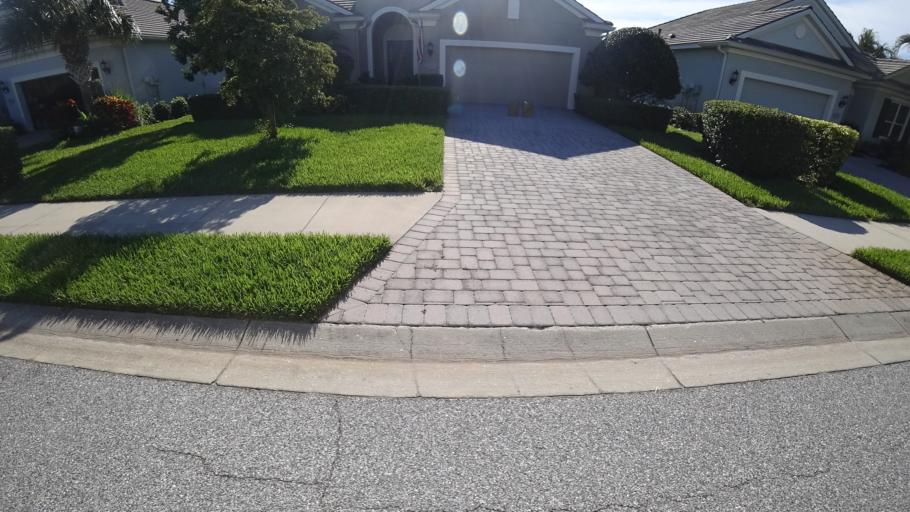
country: US
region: Florida
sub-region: Manatee County
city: West Bradenton
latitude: 27.5158
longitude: -82.6472
